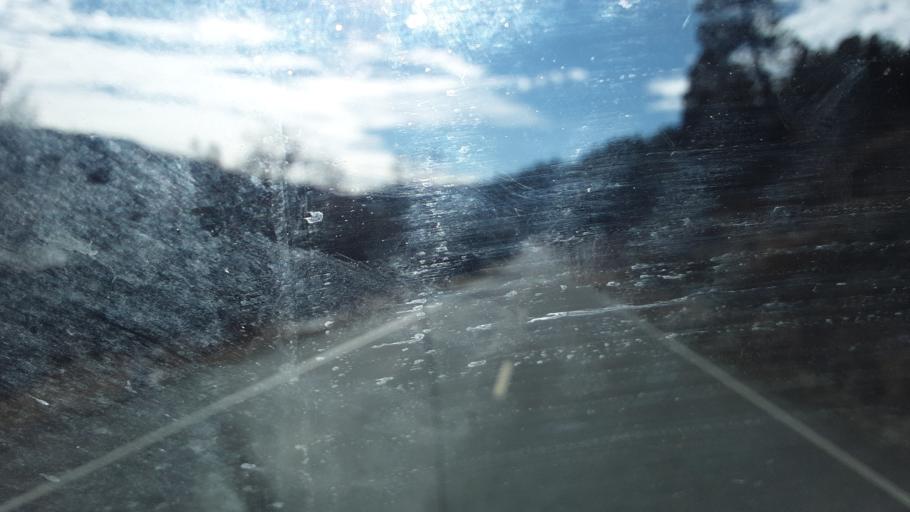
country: US
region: Colorado
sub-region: La Plata County
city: Bayfield
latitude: 37.3518
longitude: -107.6922
